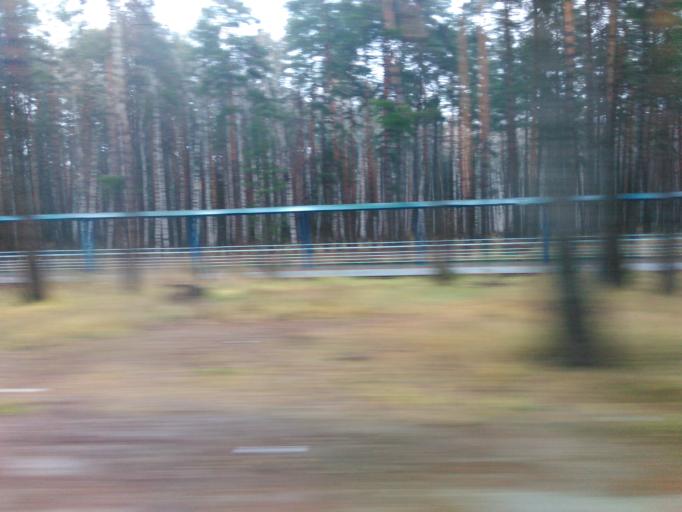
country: RU
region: Tatarstan
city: Osinovo
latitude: 55.8288
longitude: 48.8940
